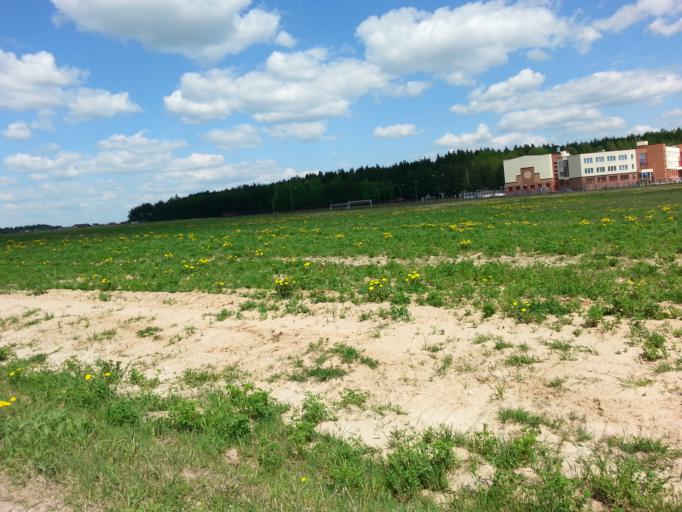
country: BY
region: Minsk
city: Narach
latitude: 54.9169
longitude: 26.6936
